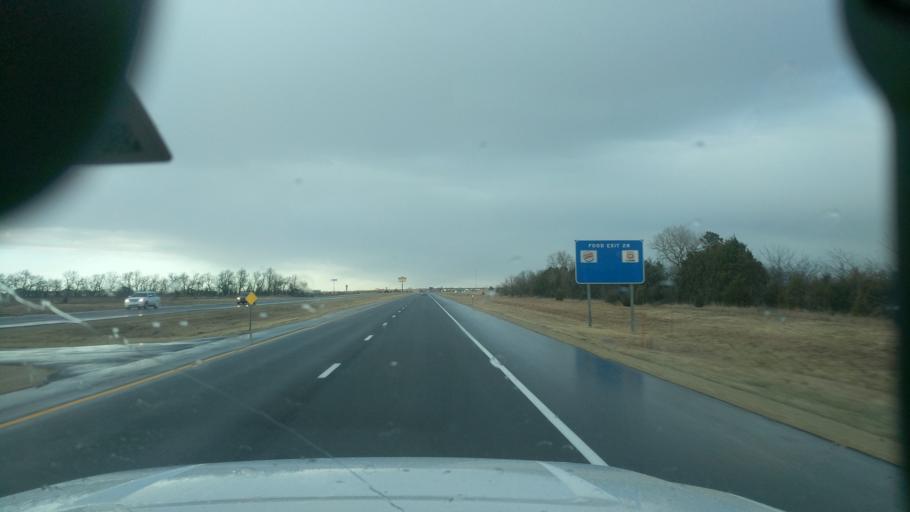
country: US
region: Kansas
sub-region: Harvey County
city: Newton
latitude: 37.9891
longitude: -97.3275
